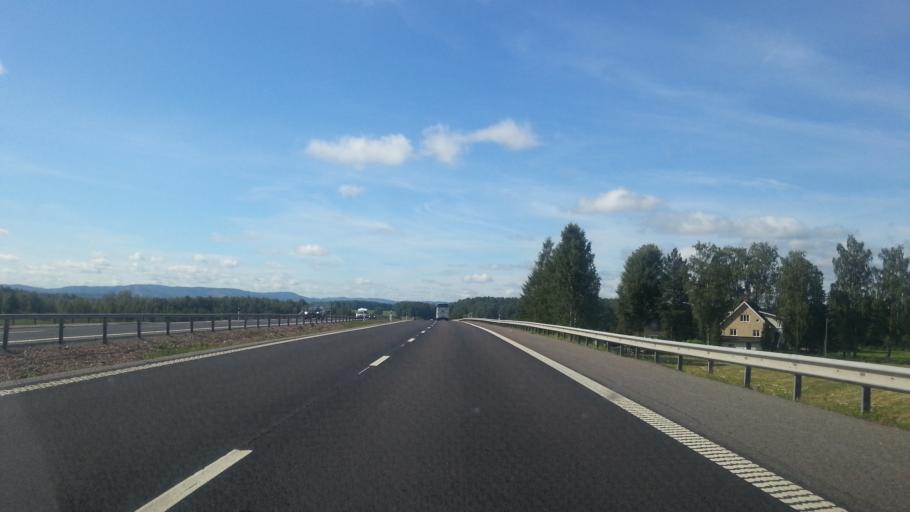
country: SE
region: Dalarna
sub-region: Borlange Kommun
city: Ornas
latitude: 60.5033
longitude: 15.5193
